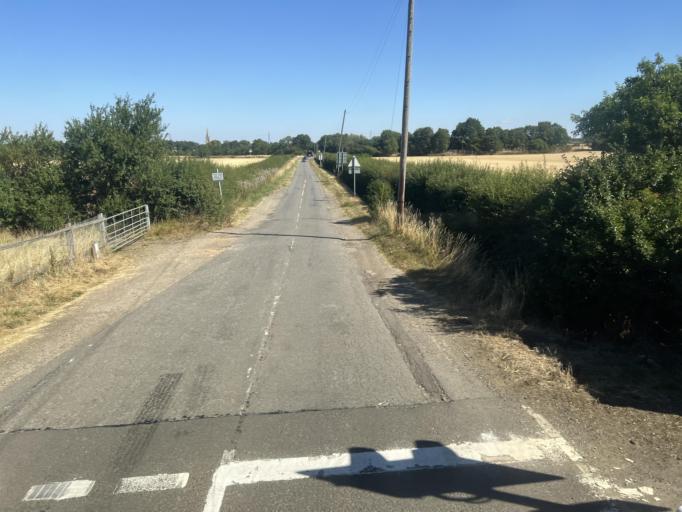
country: GB
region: England
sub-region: Lincolnshire
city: Heckington
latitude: 52.9860
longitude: -0.3392
